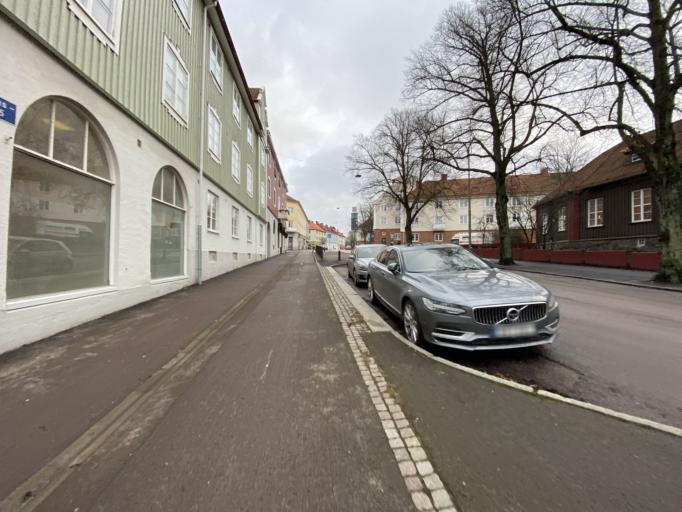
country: SE
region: Vaestra Goetaland
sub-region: Goteborg
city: Goeteborg
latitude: 57.7185
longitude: 12.0105
